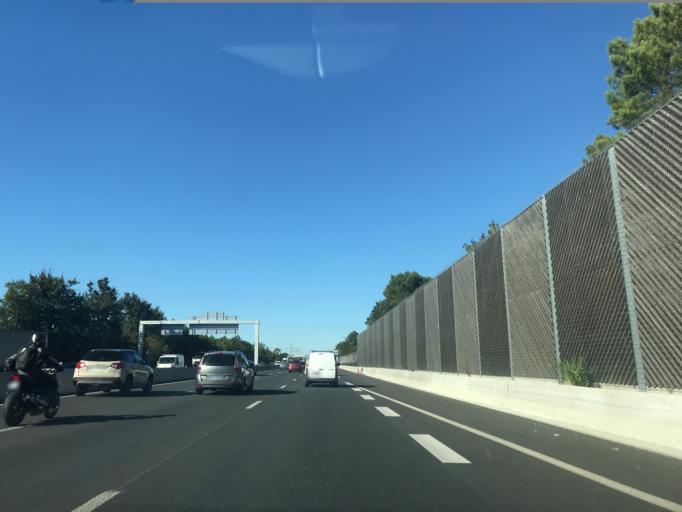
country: FR
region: Aquitaine
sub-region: Departement de la Gironde
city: Pessac
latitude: 44.8191
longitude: -0.6734
